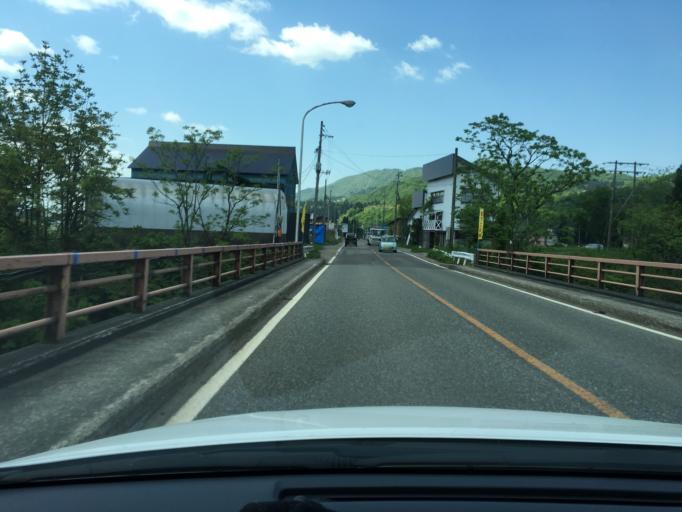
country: JP
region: Niigata
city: Tochio-honcho
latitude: 37.3376
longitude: 139.0383
